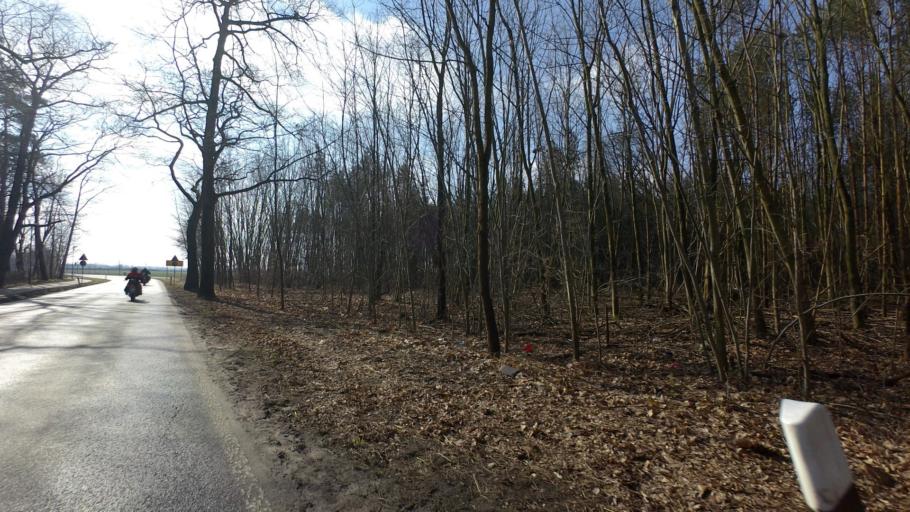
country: DE
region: Brandenburg
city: Glienicke
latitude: 52.6627
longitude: 13.3250
